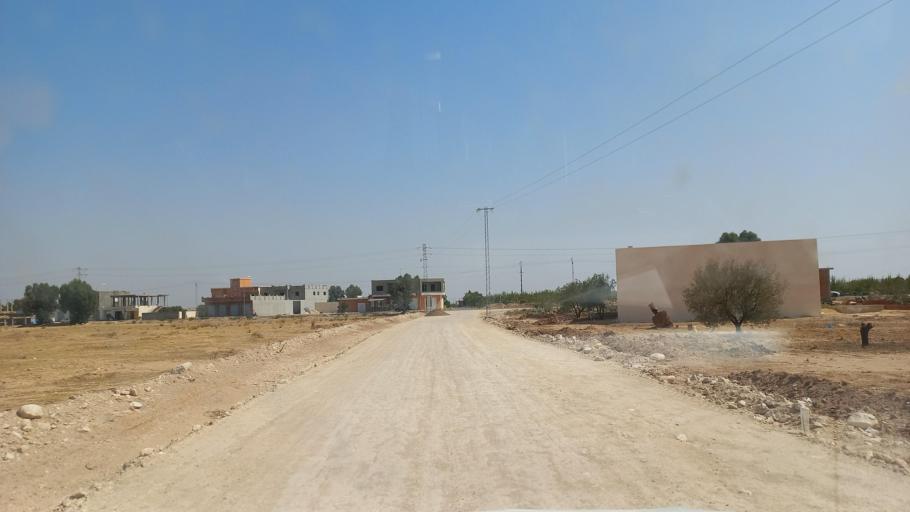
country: TN
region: Al Qasrayn
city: Kasserine
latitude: 35.2548
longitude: 9.0158
